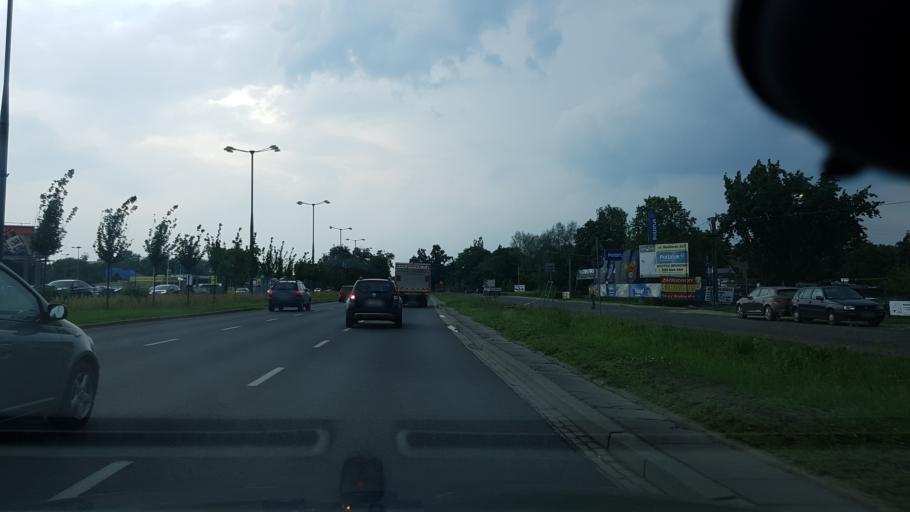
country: PL
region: Masovian Voivodeship
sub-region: Warszawa
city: Bialoleka
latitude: 52.3450
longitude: 20.9507
